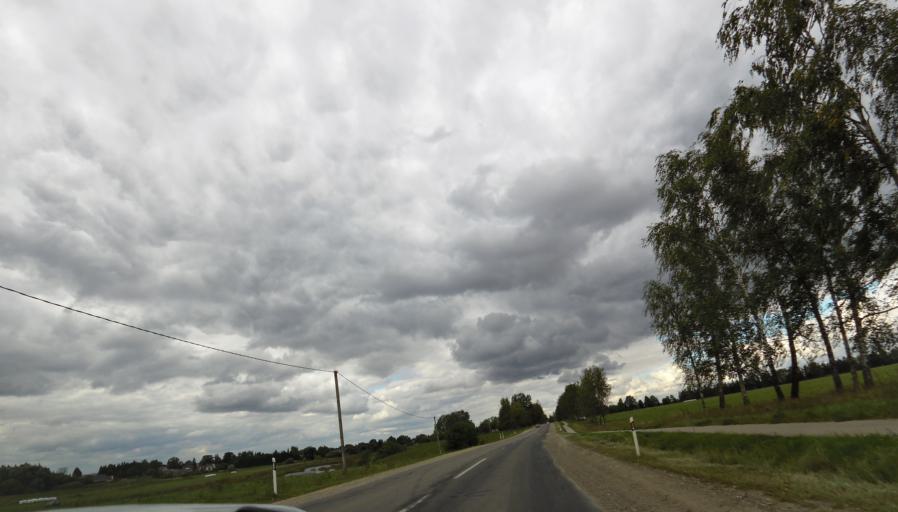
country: LT
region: Panevezys
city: Pasvalys
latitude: 56.0712
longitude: 24.3826
